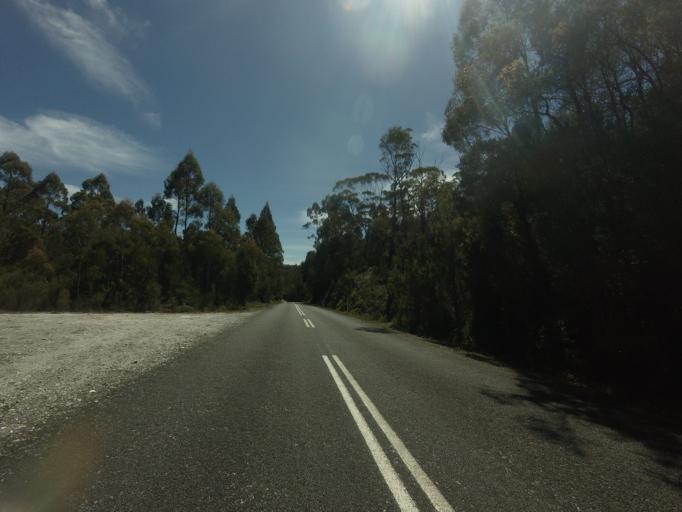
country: AU
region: Tasmania
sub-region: West Coast
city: Queenstown
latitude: -42.7734
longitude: 146.0275
